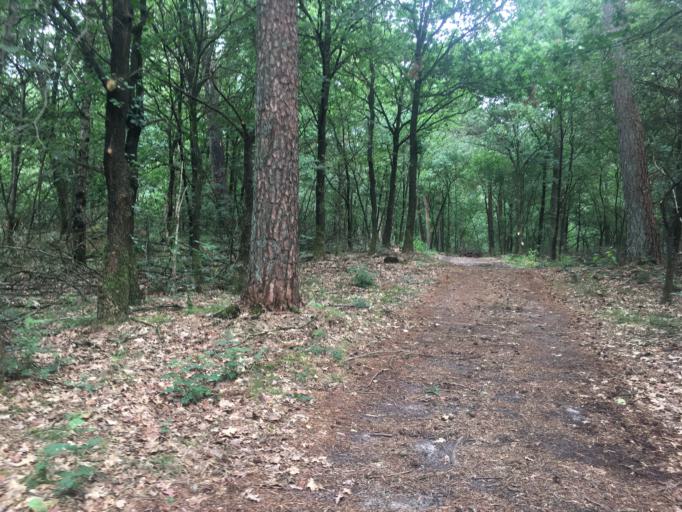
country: NL
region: Drenthe
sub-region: Gemeente Westerveld
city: Dwingeloo
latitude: 52.8871
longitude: 6.3117
